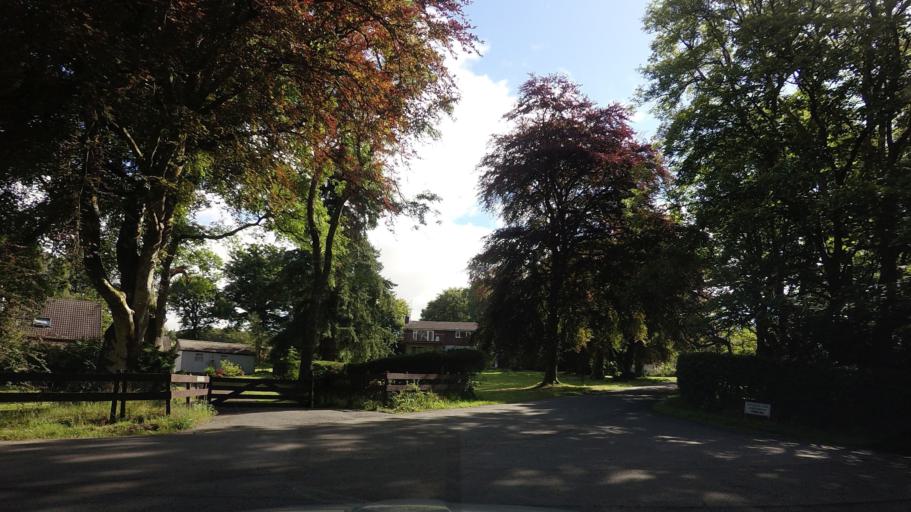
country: GB
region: Scotland
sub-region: Stirling
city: Killearn
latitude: 56.0675
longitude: -4.4772
